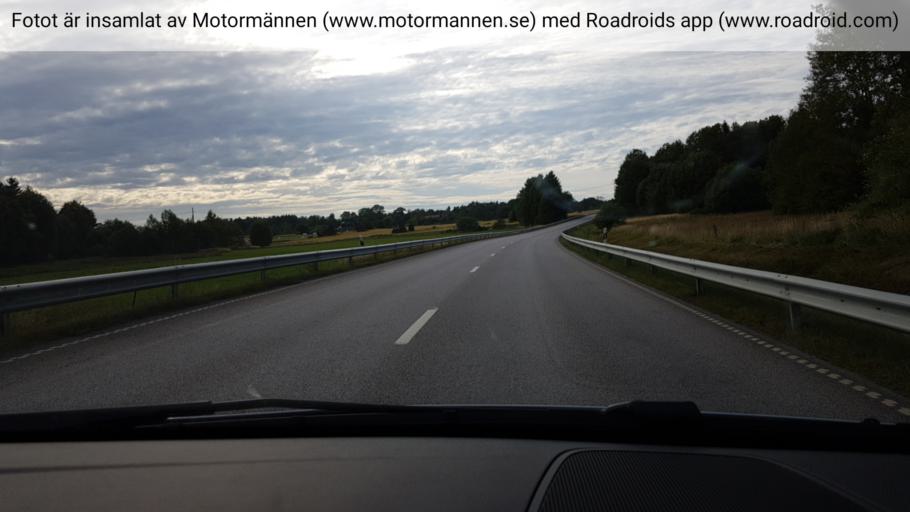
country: SE
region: Stockholm
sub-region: Norrtalje Kommun
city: Norrtalje
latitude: 59.8826
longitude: 18.6890
